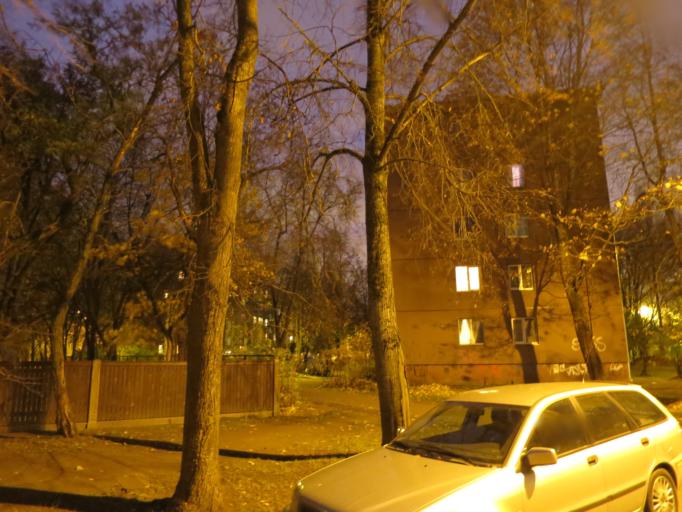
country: LV
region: Riga
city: Bergi
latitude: 56.9885
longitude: 24.2390
